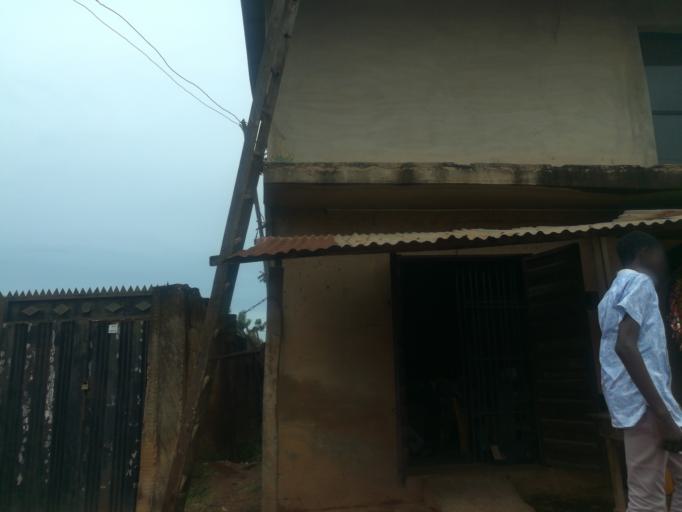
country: NG
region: Oyo
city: Ibadan
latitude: 7.3241
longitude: 3.8900
